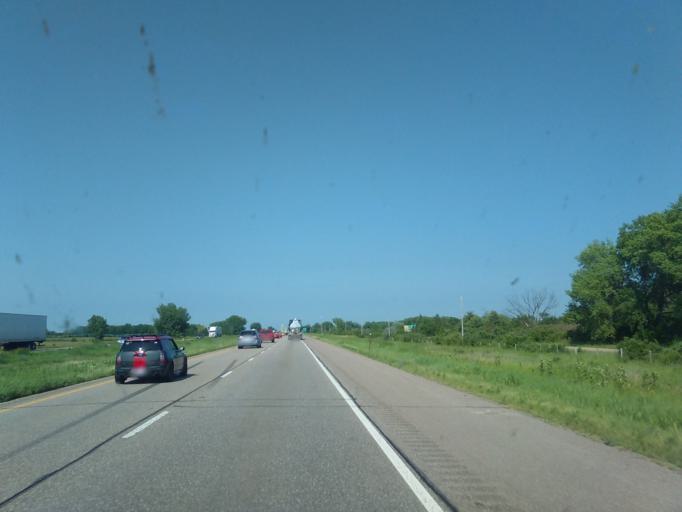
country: US
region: Nebraska
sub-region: Hall County
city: Grand Island
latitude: 40.8159
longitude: -98.4303
